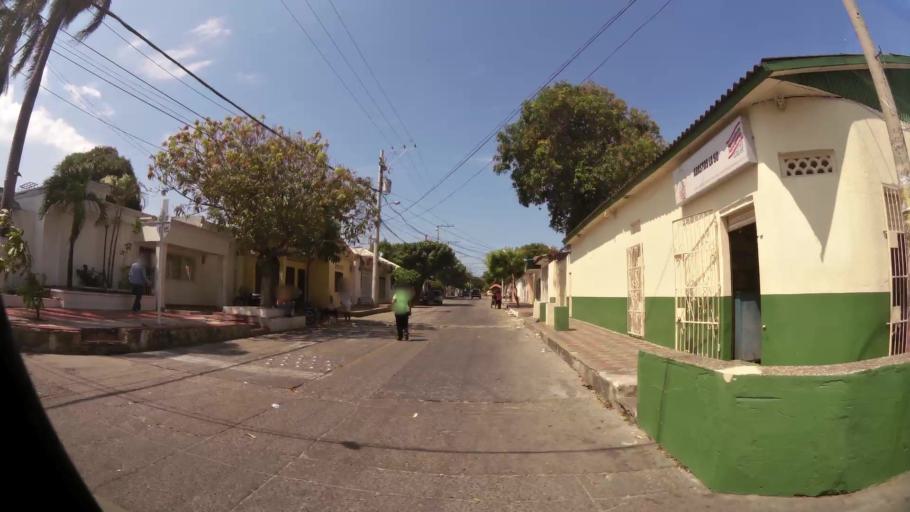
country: CO
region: Atlantico
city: Barranquilla
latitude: 10.9632
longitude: -74.8052
